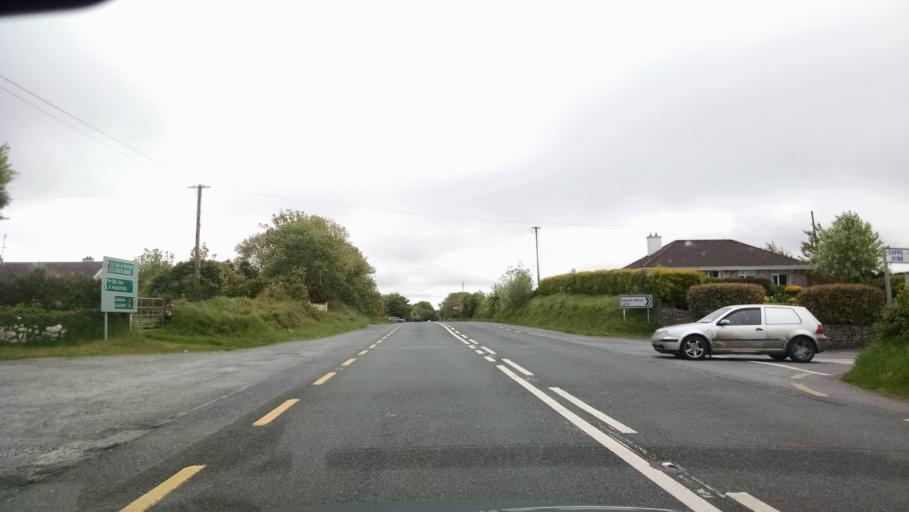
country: IE
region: Connaught
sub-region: County Galway
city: Claregalway
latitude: 53.4171
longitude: -9.0273
